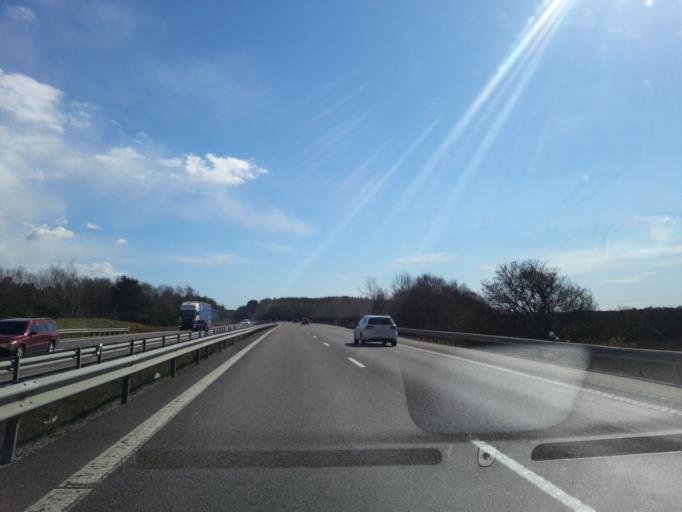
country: SE
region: Vaestra Goetaland
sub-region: Stenungsunds Kommun
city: Stora Hoga
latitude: 57.9991
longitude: 11.8433
